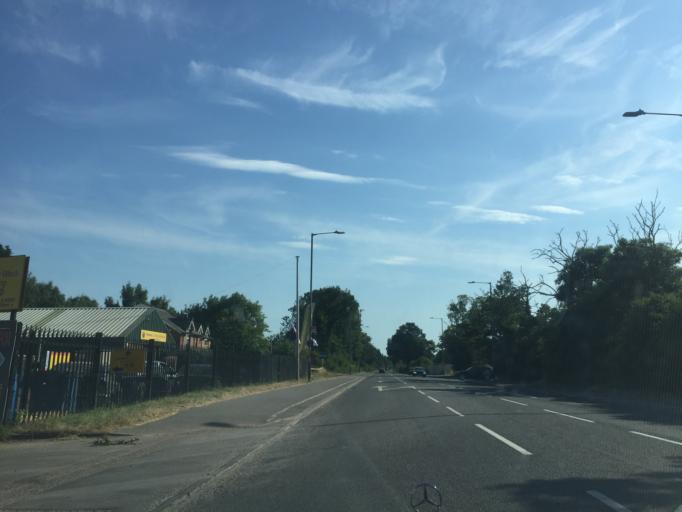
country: GB
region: England
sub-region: Warwickshire
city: Warwick
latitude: 52.2678
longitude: -1.5998
